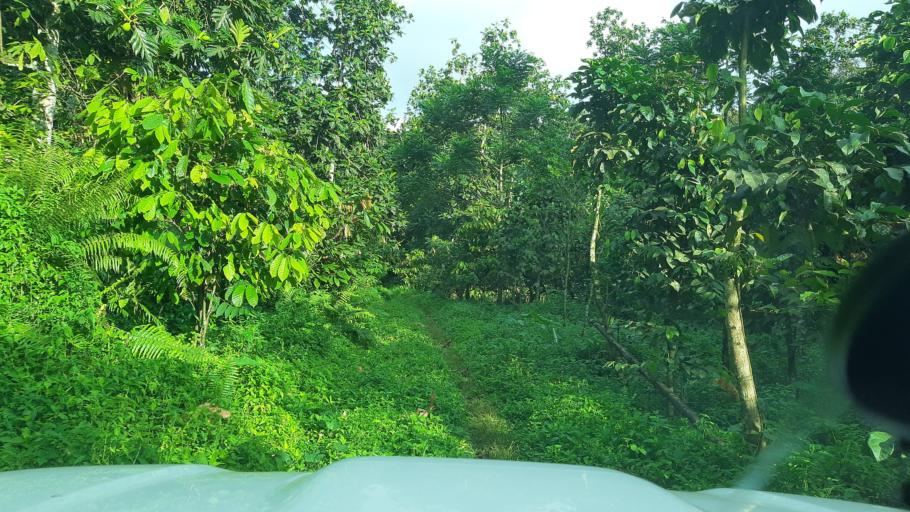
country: ST
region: Sao Tome Island
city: Sao Tome
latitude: 0.2427
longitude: 6.4690
